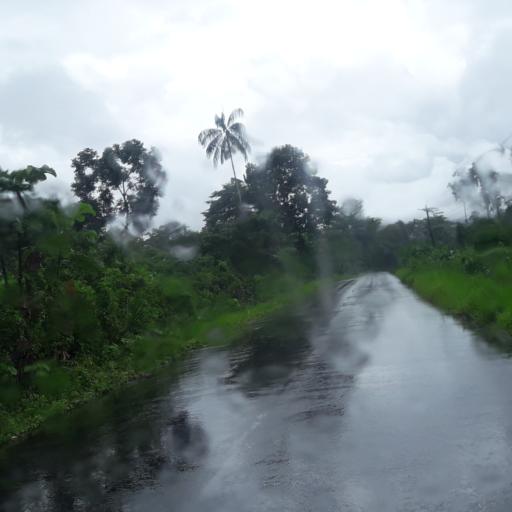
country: EC
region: Napo
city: Tena
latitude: -1.0410
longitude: -77.6639
